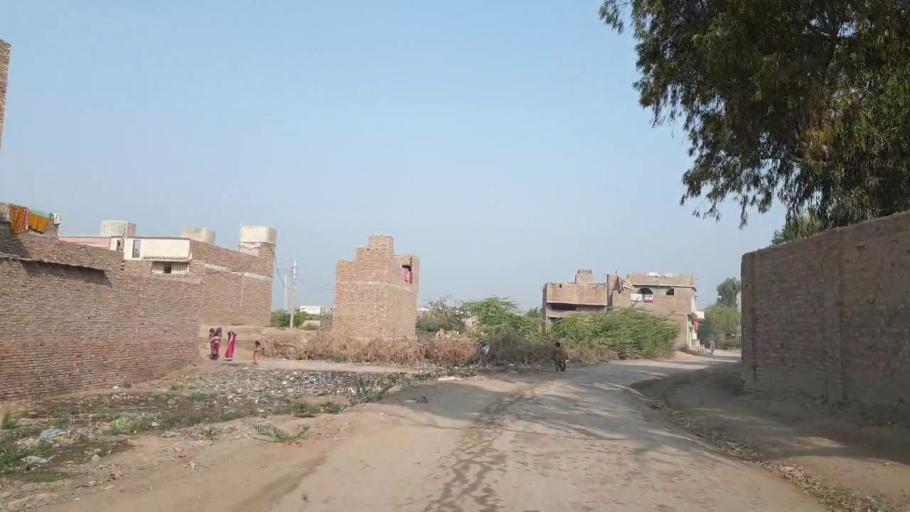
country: PK
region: Sindh
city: Mirpur Khas
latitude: 25.5399
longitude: 69.0236
